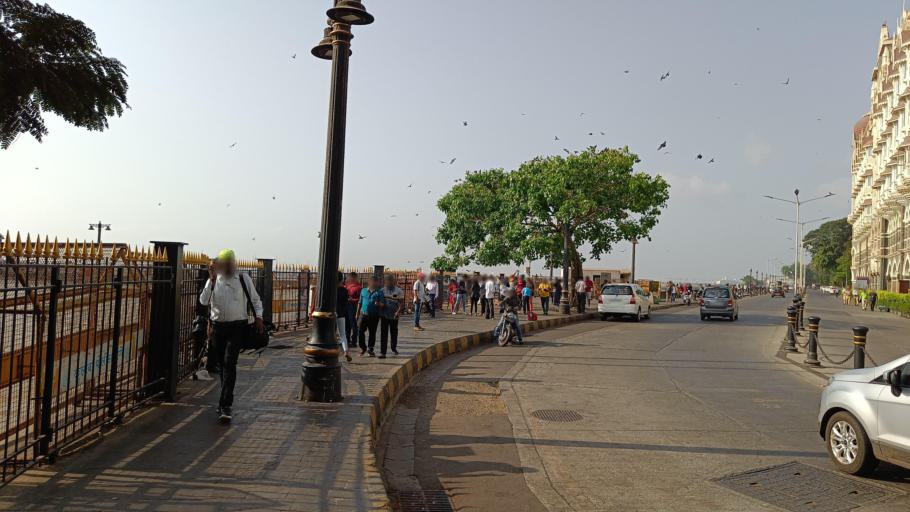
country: IN
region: Maharashtra
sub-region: Raigarh
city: Uran
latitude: 18.9224
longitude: 72.8337
